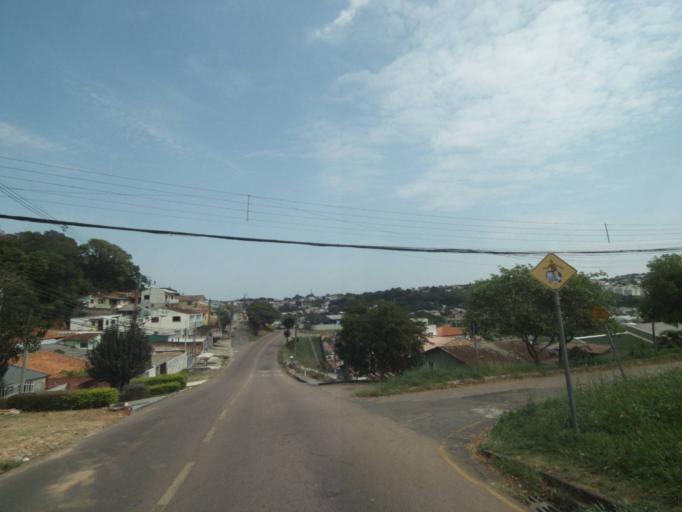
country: BR
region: Parana
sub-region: Curitiba
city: Curitiba
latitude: -25.4745
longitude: -49.3212
